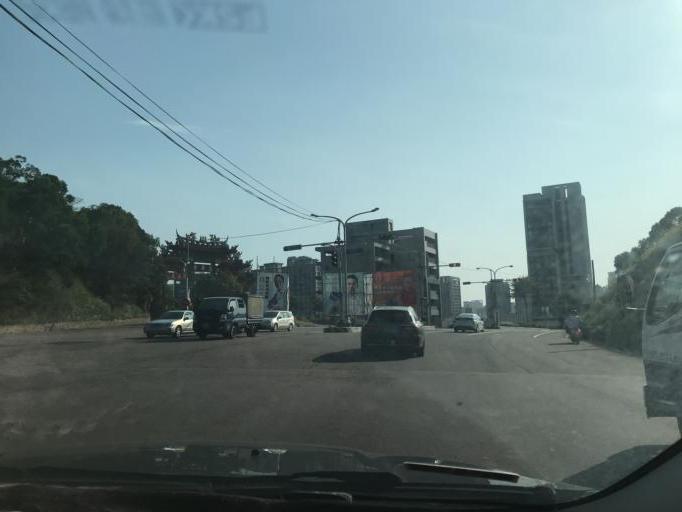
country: TW
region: Taiwan
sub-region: Hsinchu
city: Zhubei
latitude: 24.8288
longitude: 121.0356
